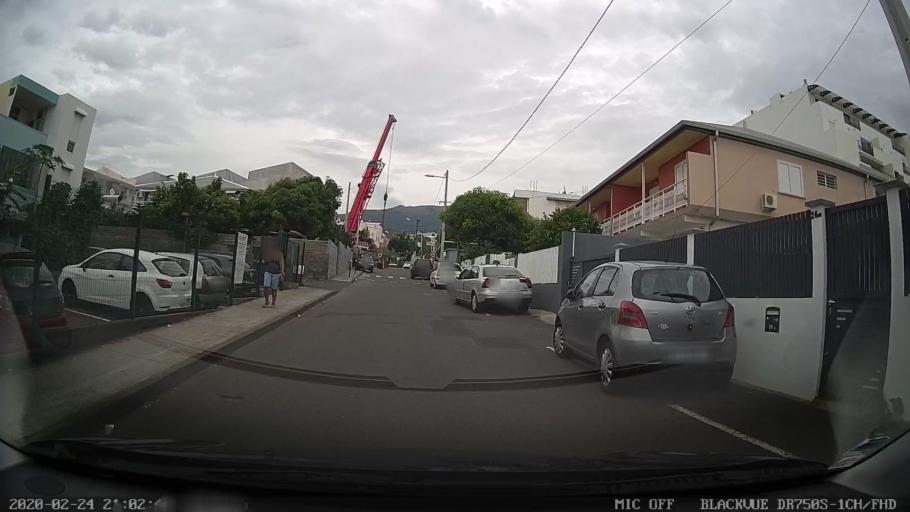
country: RE
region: Reunion
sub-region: Reunion
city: Saint-Denis
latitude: -20.8965
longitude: 55.4836
